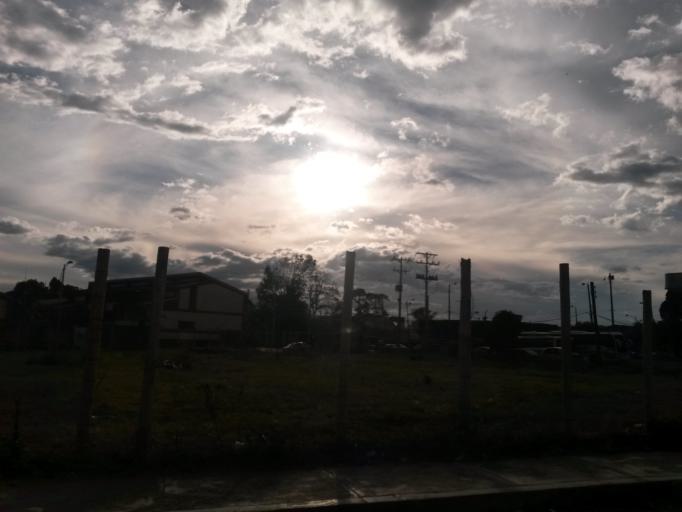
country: CO
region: Cauca
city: Popayan
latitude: 2.4492
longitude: -76.6085
